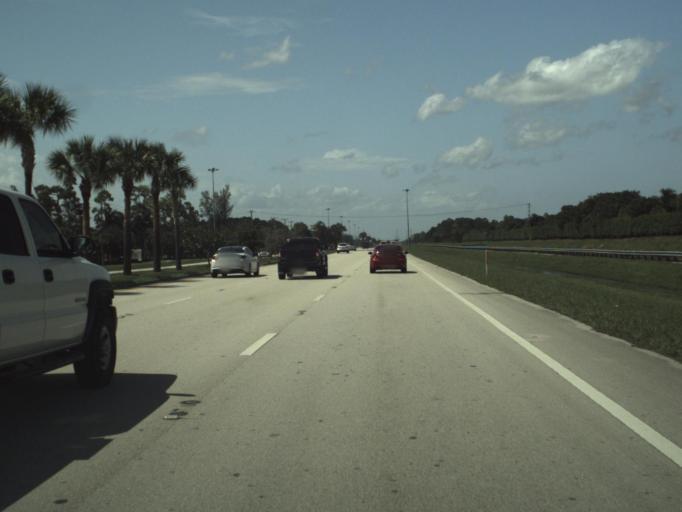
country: US
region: Florida
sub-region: Palm Beach County
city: Wellington
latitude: 26.6029
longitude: -80.2053
